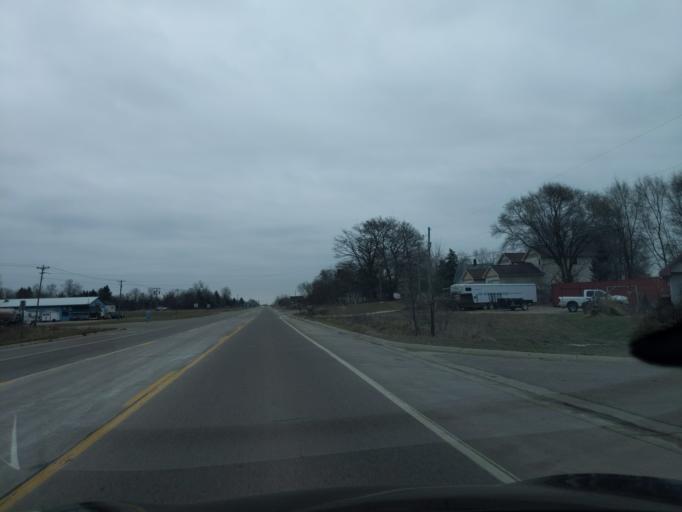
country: US
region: Michigan
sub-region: Eaton County
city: Potterville
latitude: 42.6264
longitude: -84.7342
